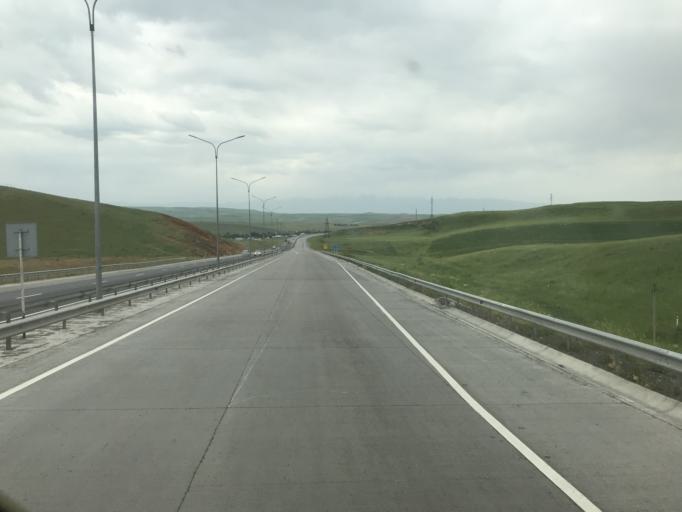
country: KZ
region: Ongtustik Qazaqstan
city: Qazyqurt
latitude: 41.9926
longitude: 69.4816
